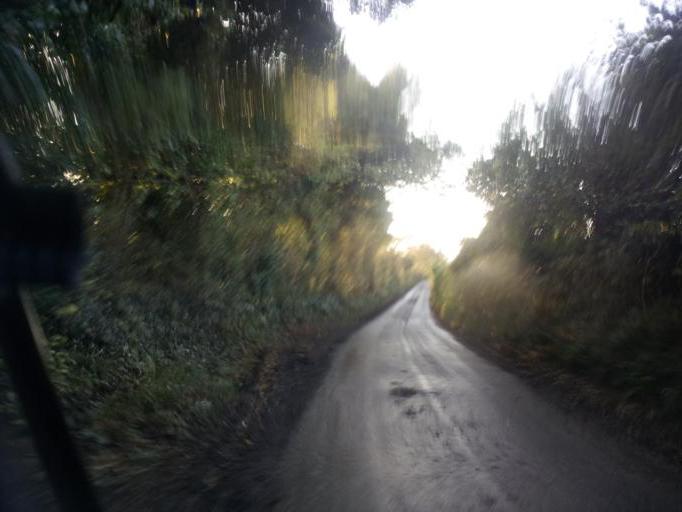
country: GB
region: England
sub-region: Kent
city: Boxley
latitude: 51.2861
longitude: 0.6043
